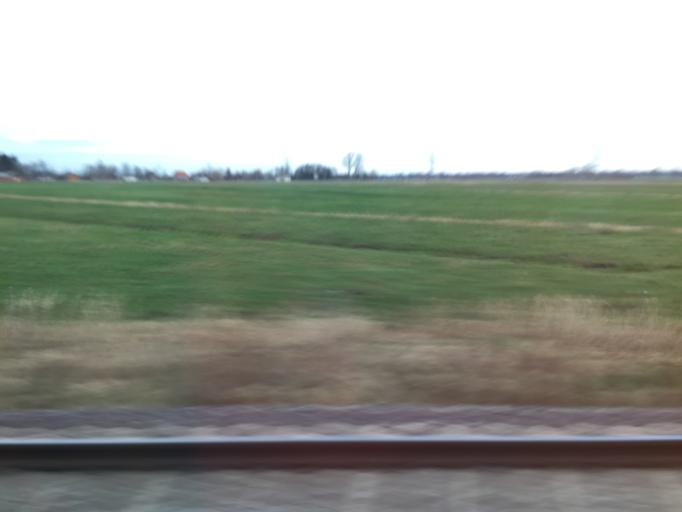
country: DE
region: Schleswig-Holstein
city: Altenmoor
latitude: 53.7860
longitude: 9.5804
